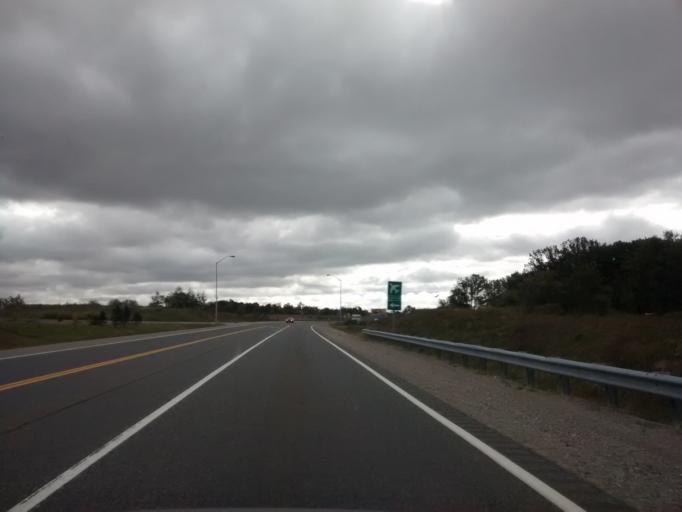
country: CA
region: Ontario
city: Ancaster
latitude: 43.1555
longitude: -79.9344
